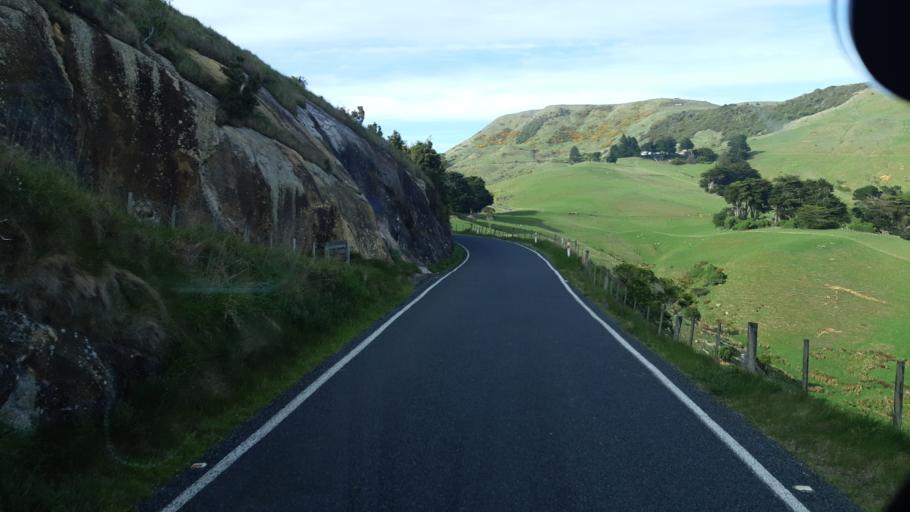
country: NZ
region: Otago
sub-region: Dunedin City
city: Portobello
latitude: -45.8590
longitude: 170.6424
